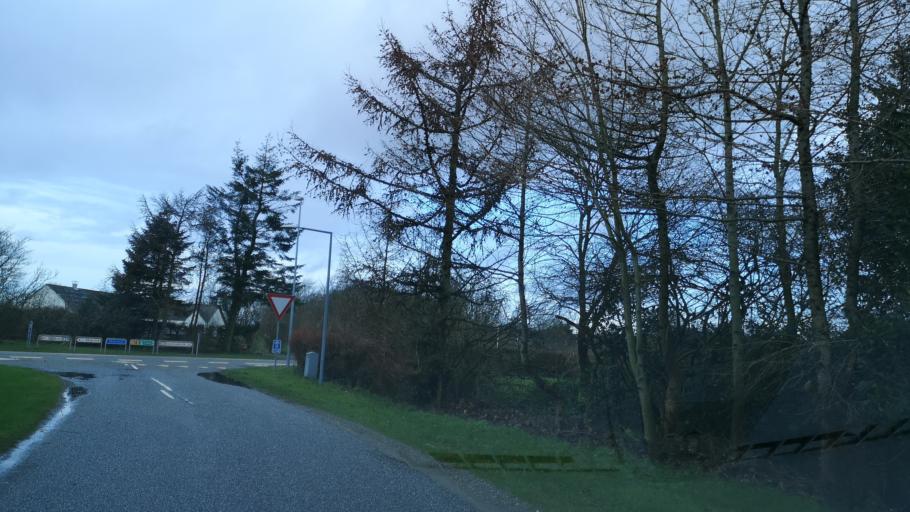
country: DK
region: Central Jutland
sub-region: Herning Kommune
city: Lind
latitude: 56.0103
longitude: 8.9803
